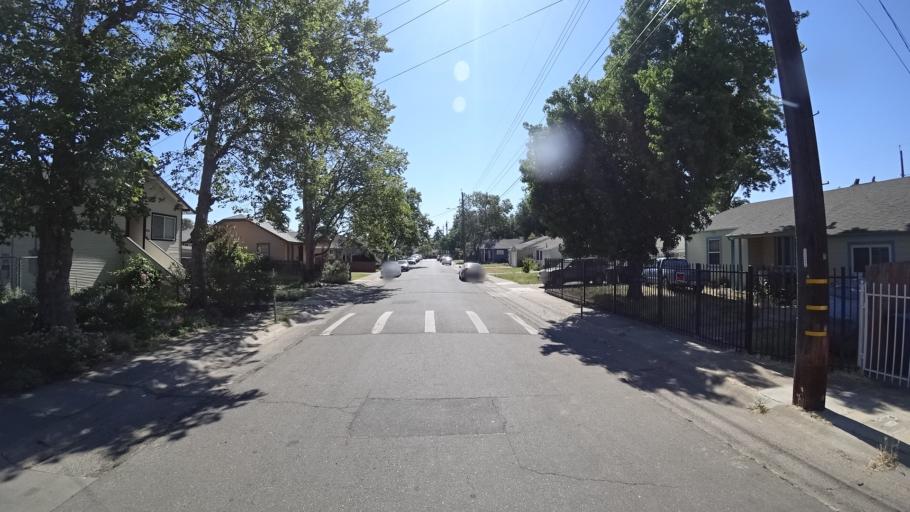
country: US
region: California
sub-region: Sacramento County
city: Parkway
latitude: 38.5420
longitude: -121.4534
